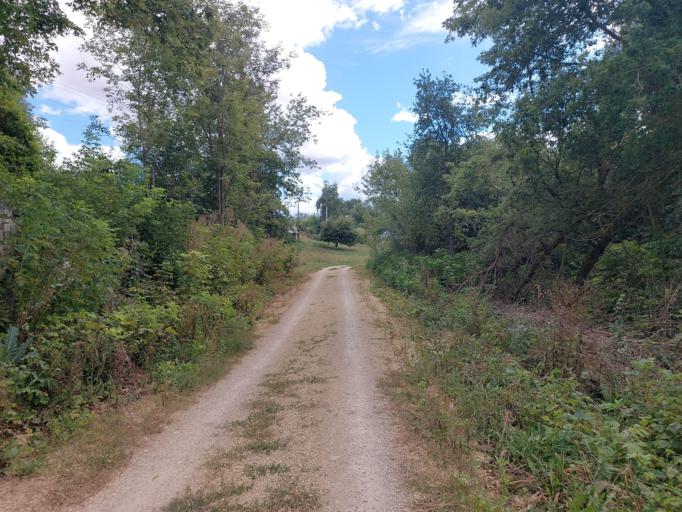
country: RU
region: Lipetsk
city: Terbuny
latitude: 52.2603
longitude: 38.2076
